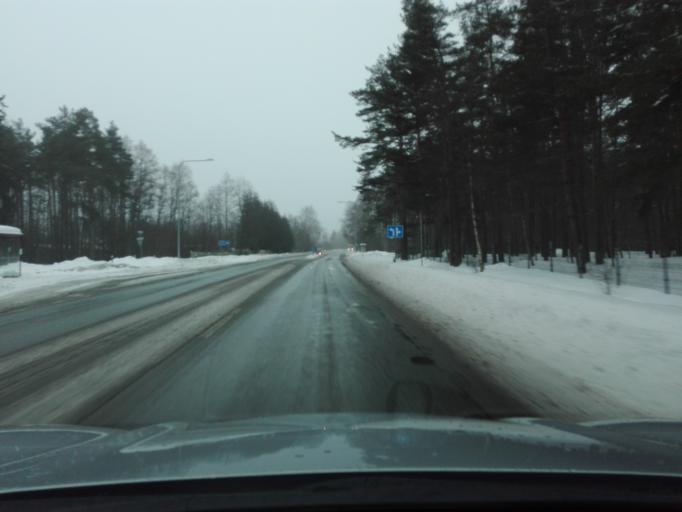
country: EE
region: Harju
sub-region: Kiili vald
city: Kiili
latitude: 59.3336
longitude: 24.7737
